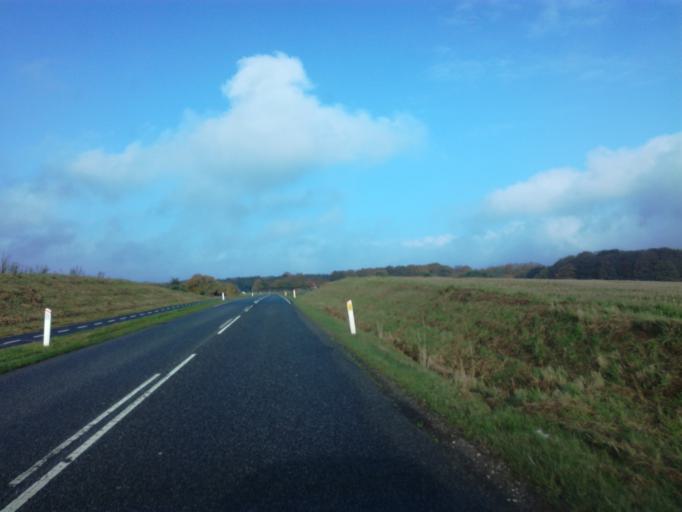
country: DK
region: South Denmark
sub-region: Vejle Kommune
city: Borkop
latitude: 55.6705
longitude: 9.6198
